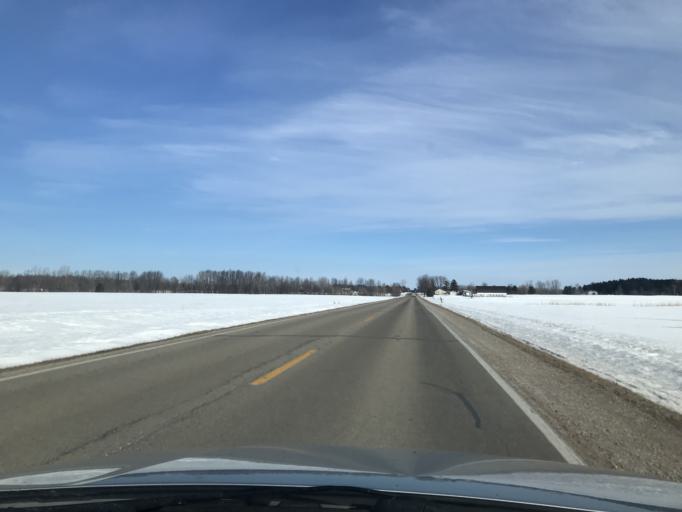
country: US
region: Wisconsin
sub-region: Oconto County
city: Oconto Falls
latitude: 44.8917
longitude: -88.1562
